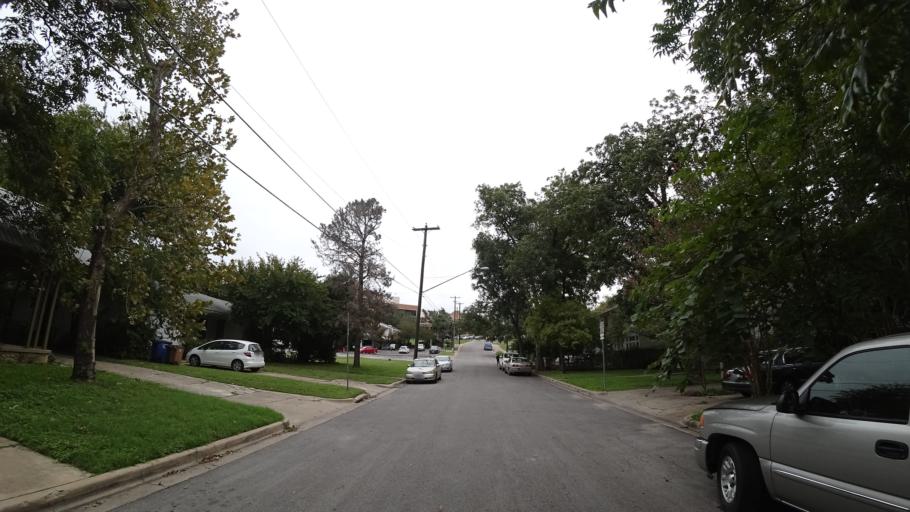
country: US
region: Texas
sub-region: Travis County
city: Austin
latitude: 30.2908
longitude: -97.7289
